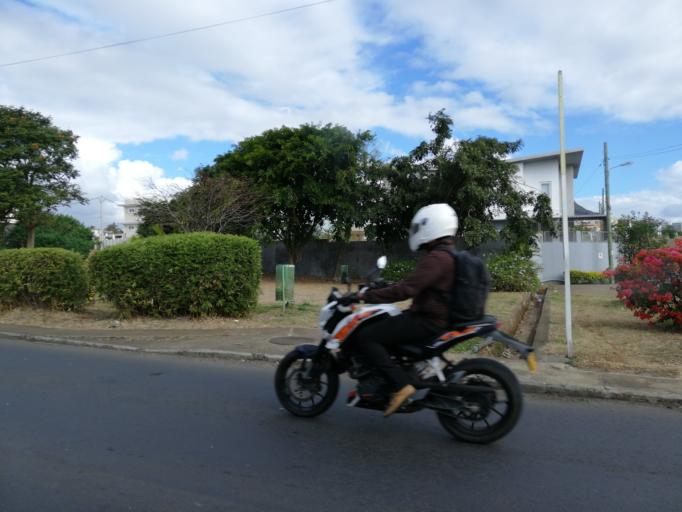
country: MU
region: Black River
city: Gros Cailloux
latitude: -20.2309
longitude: 57.4514
